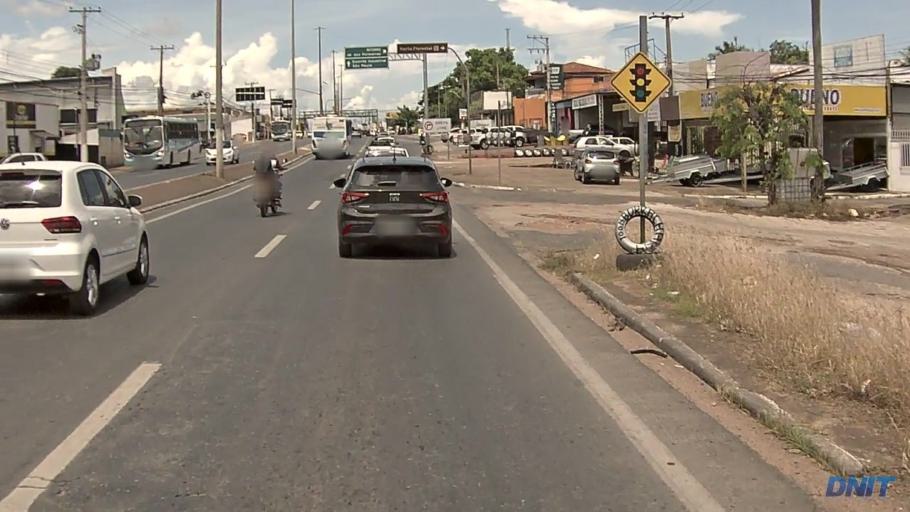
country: BR
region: Mato Grosso
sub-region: Cuiaba
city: Cuiaba
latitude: -15.6259
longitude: -56.0595
